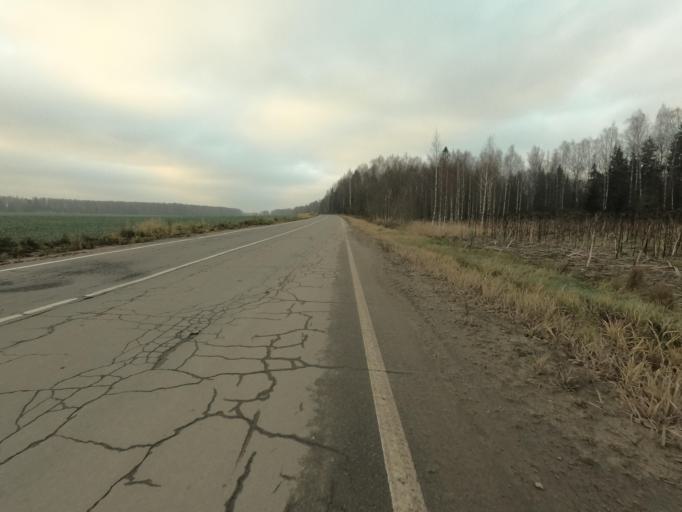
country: RU
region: Leningrad
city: Mga
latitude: 59.7954
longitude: 31.0056
